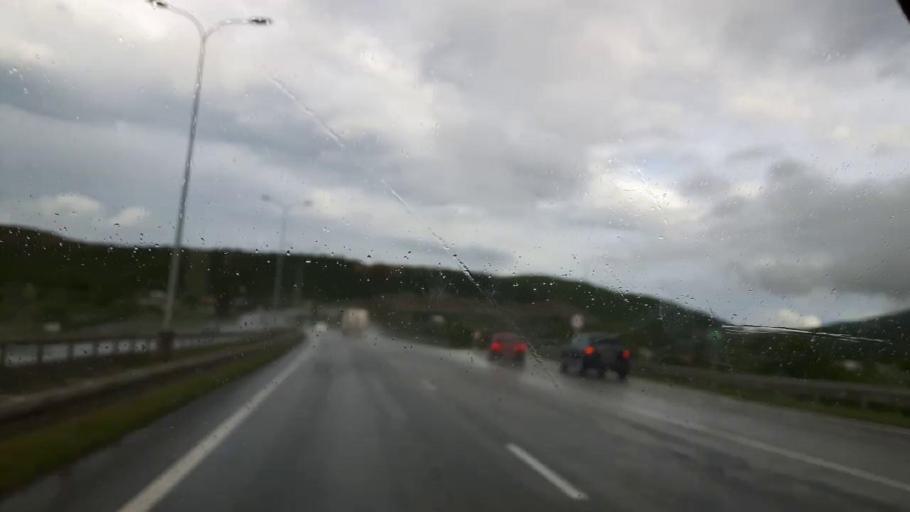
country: GE
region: Shida Kartli
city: Kaspi
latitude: 41.9949
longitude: 44.4147
